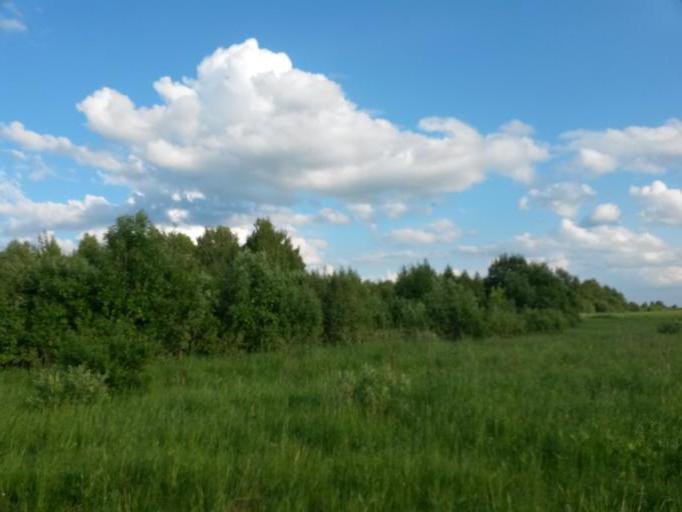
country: RU
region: Jaroslavl
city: Burmakino
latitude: 57.3701
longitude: 40.2016
